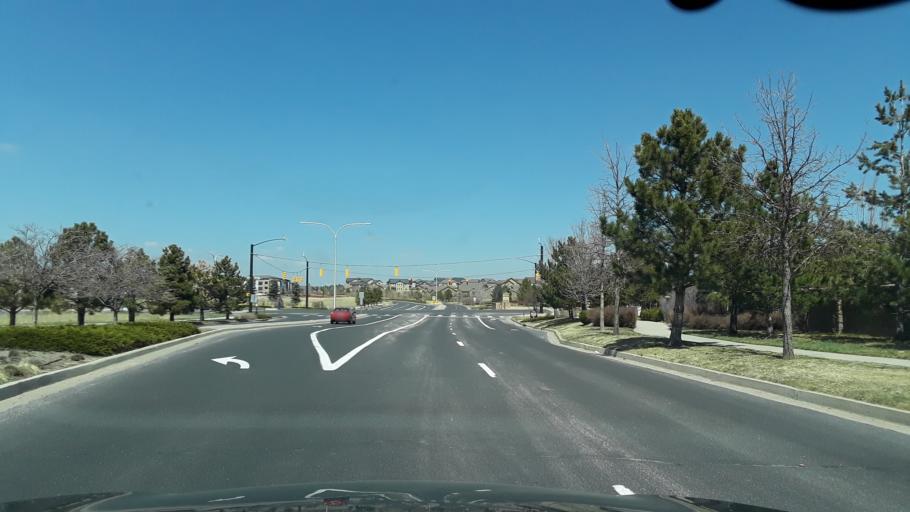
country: US
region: Colorado
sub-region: El Paso County
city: Black Forest
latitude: 38.9699
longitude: -104.7382
